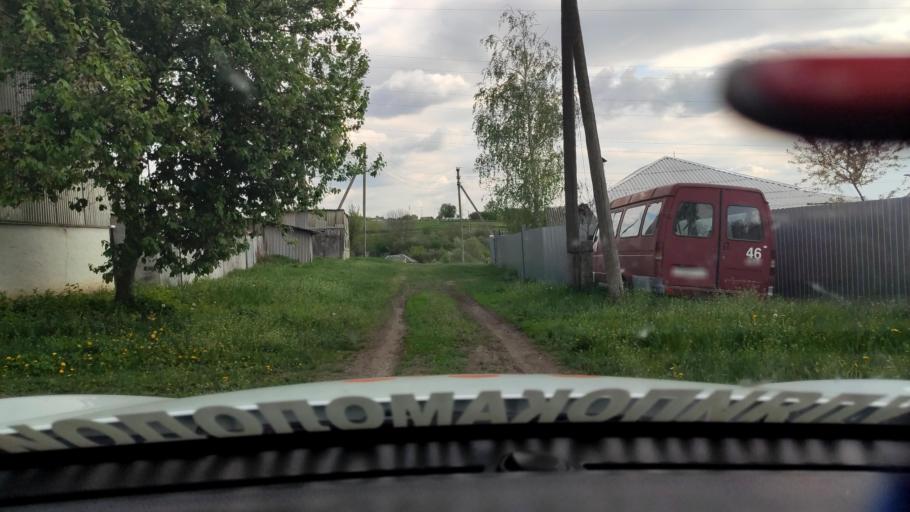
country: RU
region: Voronezj
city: Uryv-Pokrovka
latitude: 51.1177
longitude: 39.1671
